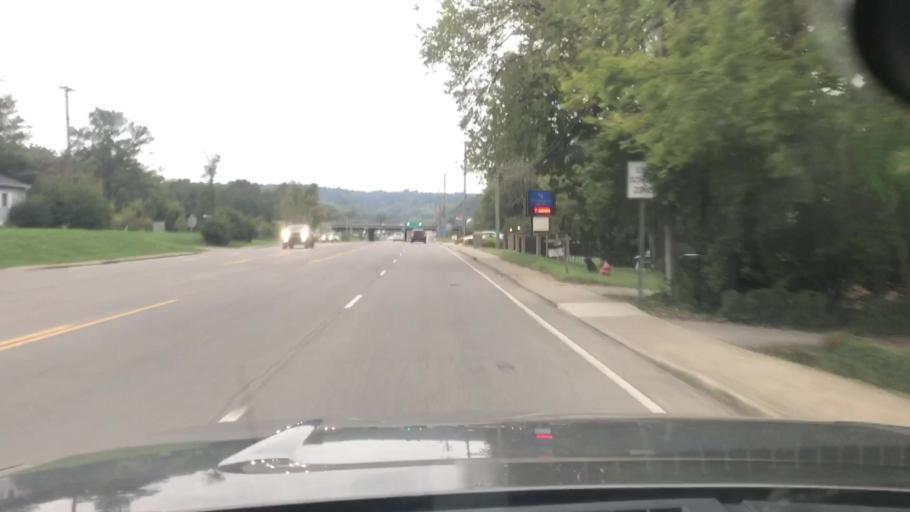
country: US
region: Tennessee
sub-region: Davidson County
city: Belle Meade
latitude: 36.1147
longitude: -86.9231
